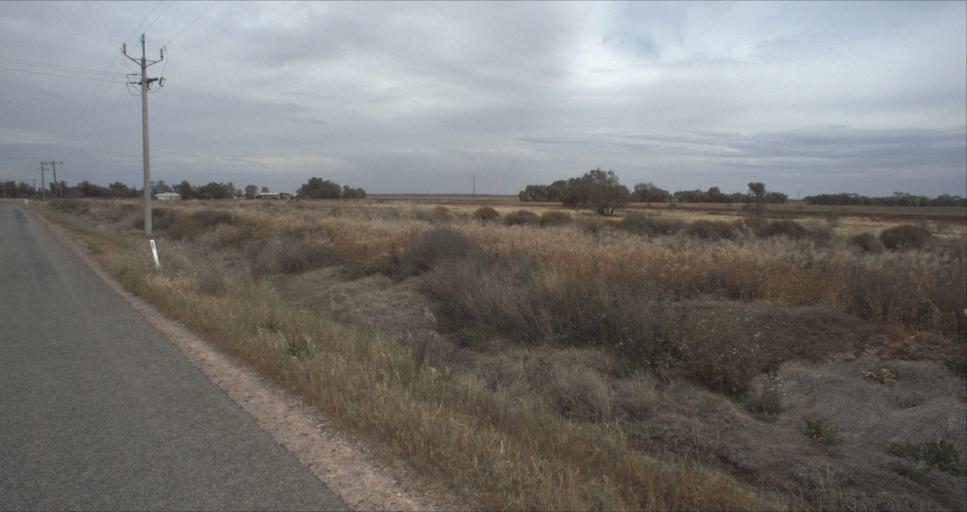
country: AU
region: New South Wales
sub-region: Leeton
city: Leeton
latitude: -34.4385
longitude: 146.3760
